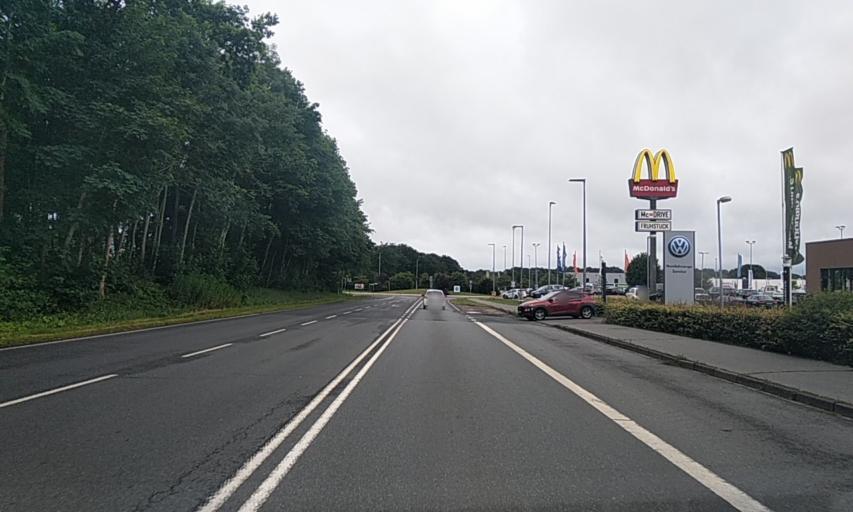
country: DE
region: Schleswig-Holstein
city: Schleswig
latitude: 54.5305
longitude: 9.5759
